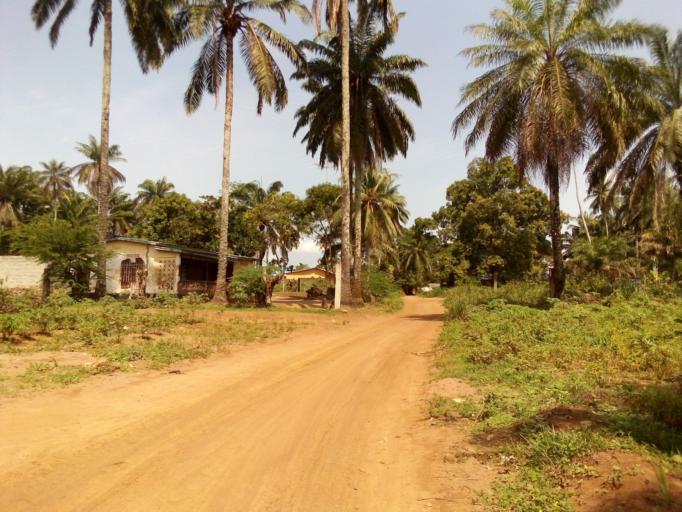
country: SL
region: Western Area
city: Waterloo
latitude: 8.3385
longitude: -13.0069
